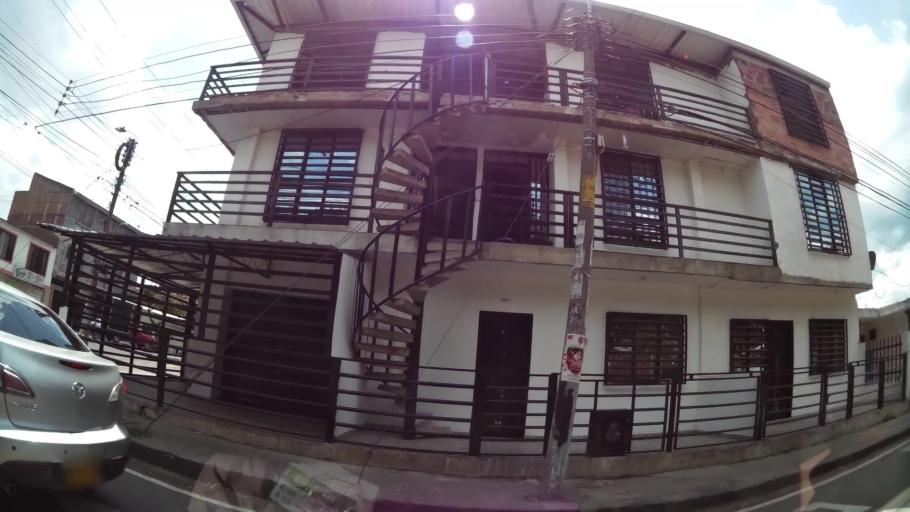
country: CO
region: Valle del Cauca
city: Cali
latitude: 3.4649
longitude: -76.5038
